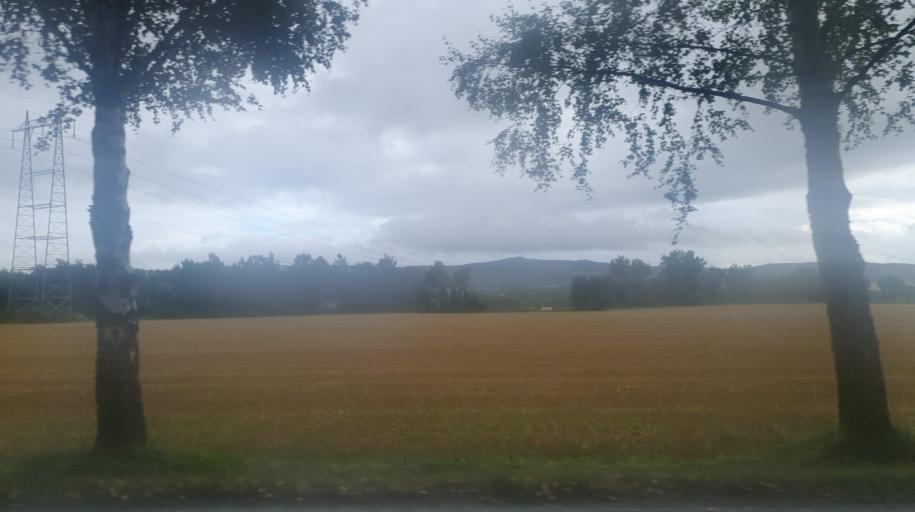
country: NO
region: Nord-Trondelag
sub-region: Verdal
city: Verdal
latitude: 63.7956
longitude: 11.5200
